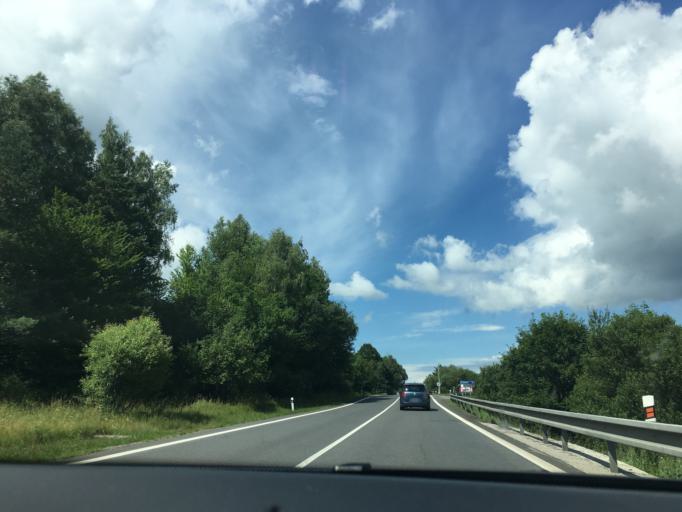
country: PL
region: Subcarpathian Voivodeship
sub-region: Powiat krosnienski
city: Jasliska
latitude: 49.3707
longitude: 21.6926
